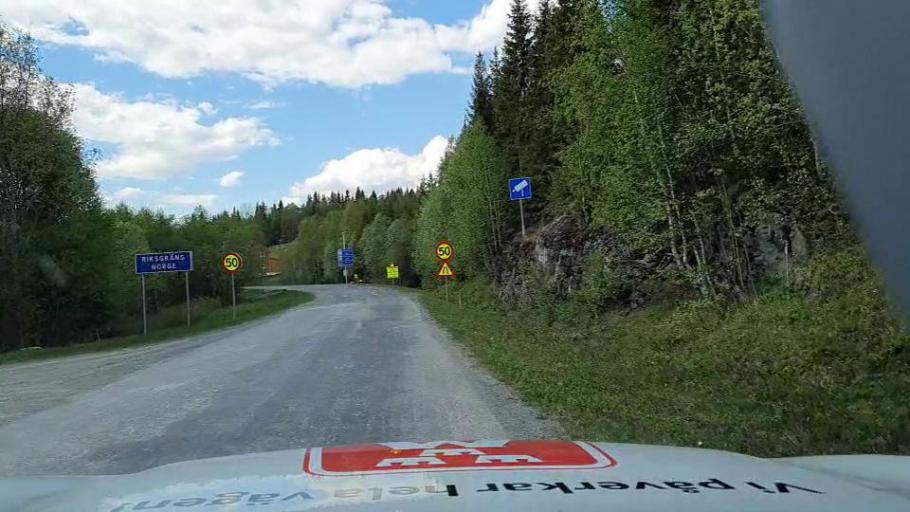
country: NO
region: Nord-Trondelag
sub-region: Lierne
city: Sandvika
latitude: 64.1344
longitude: 14.0973
